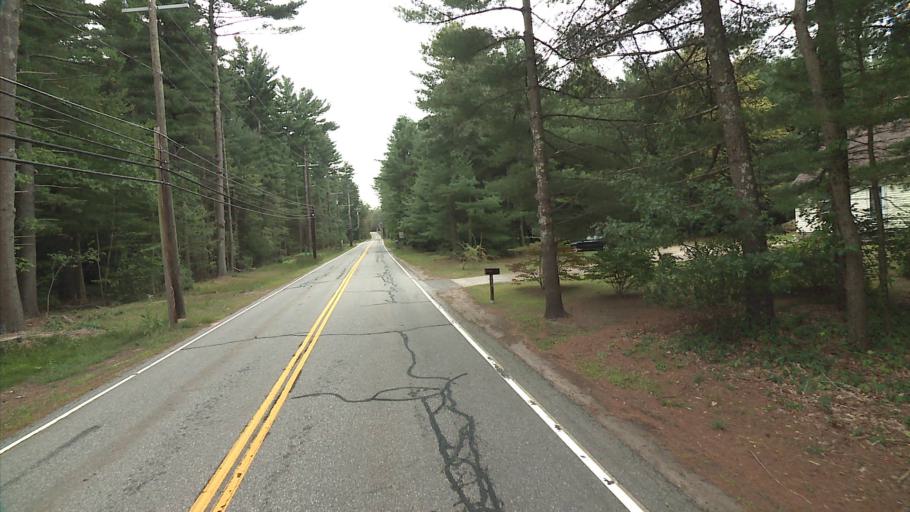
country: US
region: Connecticut
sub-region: Tolland County
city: Storrs
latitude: 41.8430
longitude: -72.2726
